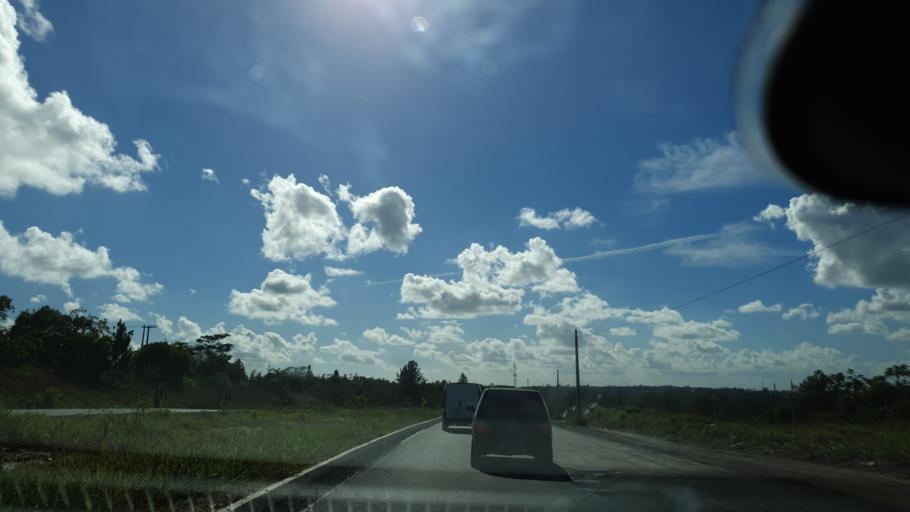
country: BR
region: Bahia
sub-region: Camacari
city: Camacari
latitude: -12.6823
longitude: -38.2900
